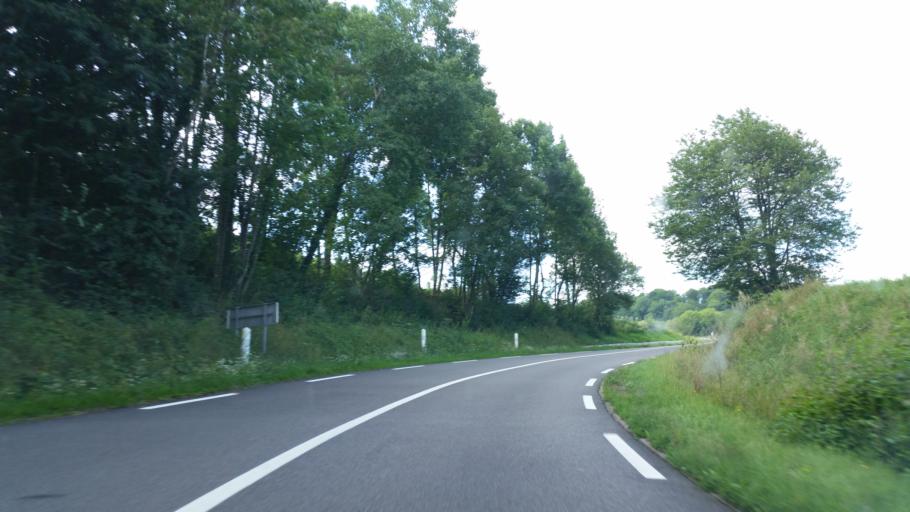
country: FR
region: Franche-Comte
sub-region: Departement du Doubs
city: Saint-Hippolyte
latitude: 47.3045
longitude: 6.8083
